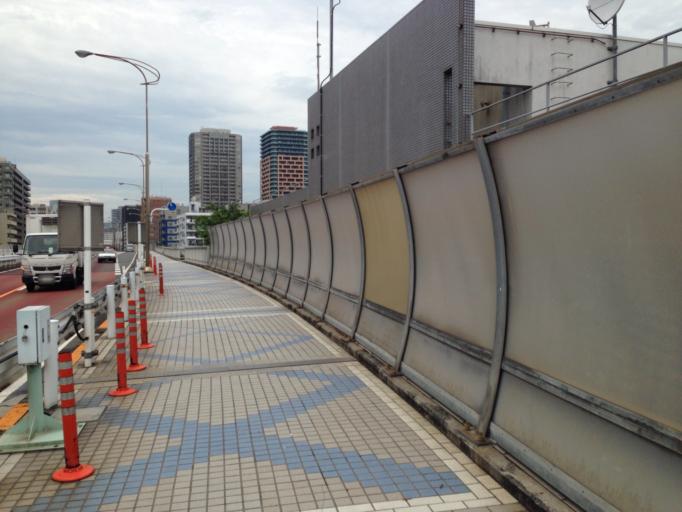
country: JP
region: Tokyo
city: Tokyo
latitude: 35.6618
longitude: 139.7877
